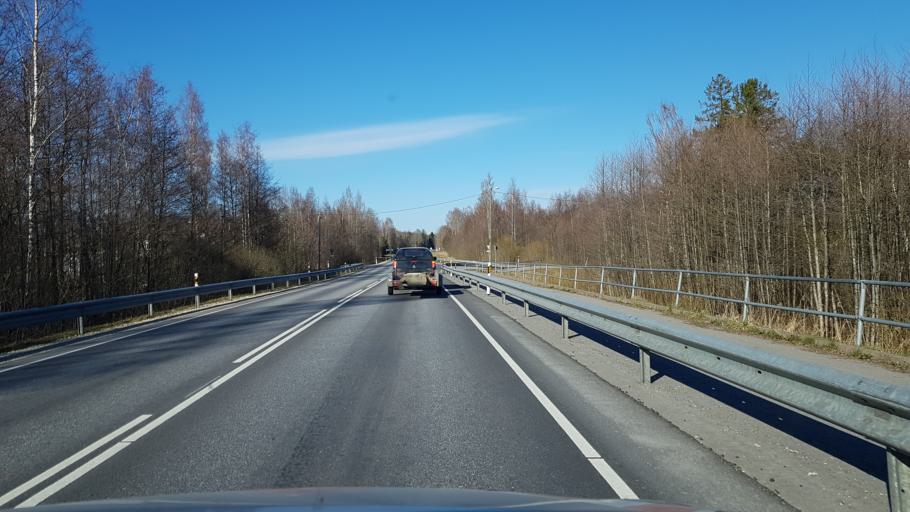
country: EE
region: Jogevamaa
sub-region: Mustvee linn
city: Mustvee
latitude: 58.9473
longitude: 27.0550
